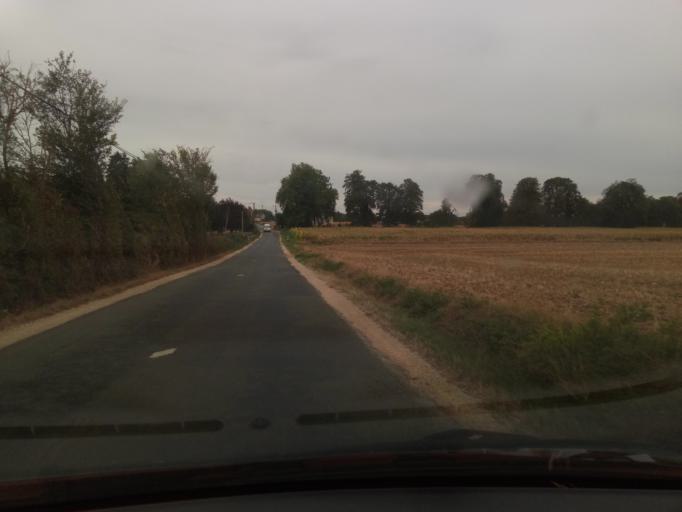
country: FR
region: Poitou-Charentes
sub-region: Departement de la Vienne
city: Saint-Savin
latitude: 46.5152
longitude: 0.7743
